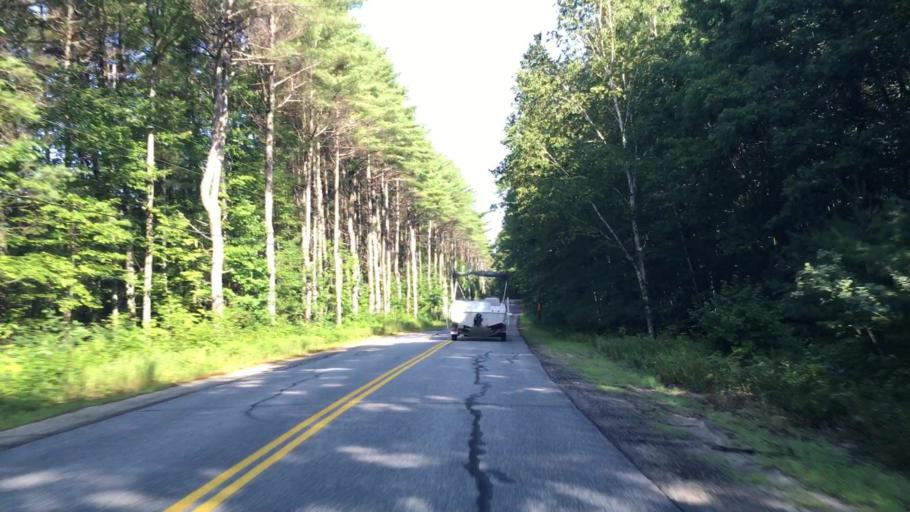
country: US
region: Maine
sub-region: Androscoggin County
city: Poland
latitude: 44.0548
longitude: -70.3776
